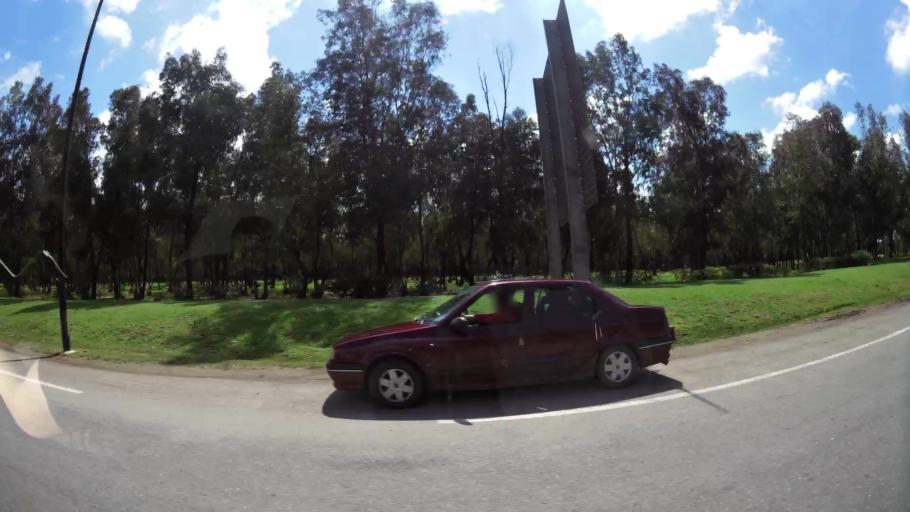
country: MA
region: Chaouia-Ouardigha
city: Nouaseur
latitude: 33.3801
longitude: -7.5715
